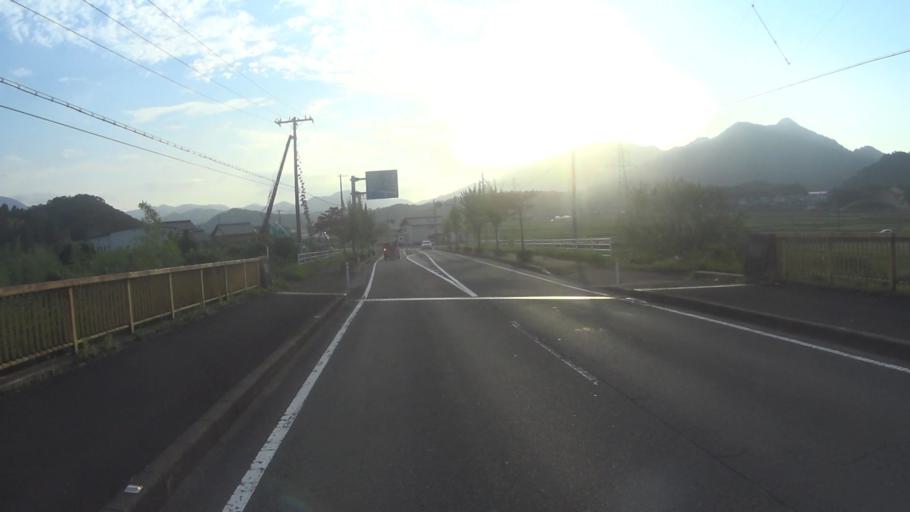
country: JP
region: Kyoto
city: Miyazu
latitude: 35.6020
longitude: 135.0482
